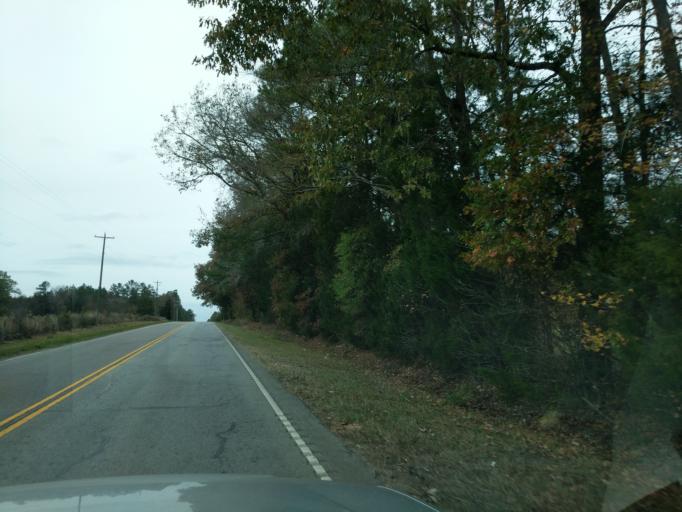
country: US
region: South Carolina
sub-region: Saluda County
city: Saluda
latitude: 34.0250
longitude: -81.7685
